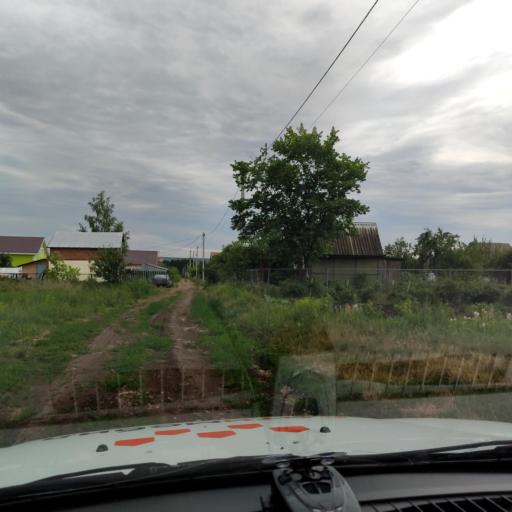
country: RU
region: Bashkortostan
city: Avdon
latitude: 54.5181
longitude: 55.8202
